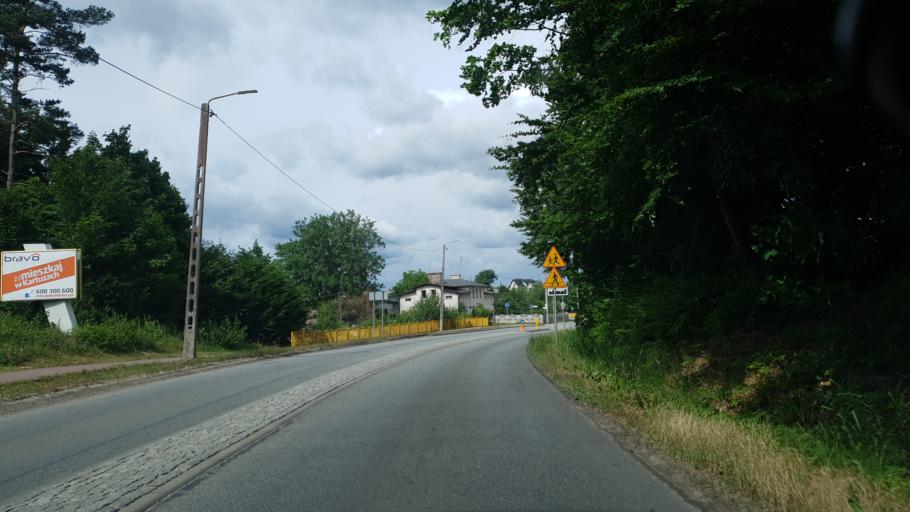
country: PL
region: Pomeranian Voivodeship
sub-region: Powiat kartuski
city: Kartuzy
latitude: 54.3504
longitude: 18.2168
